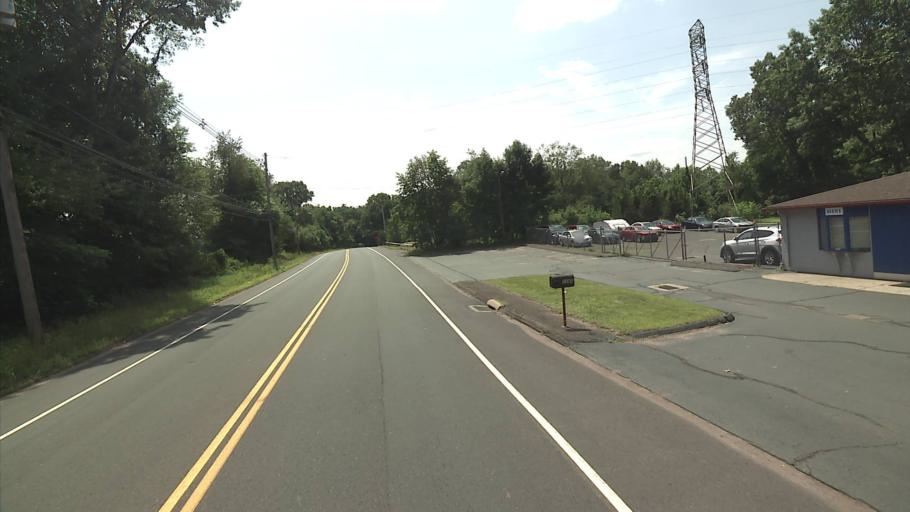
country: US
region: Connecticut
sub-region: New Haven County
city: Meriden
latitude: 41.5001
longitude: -72.8160
